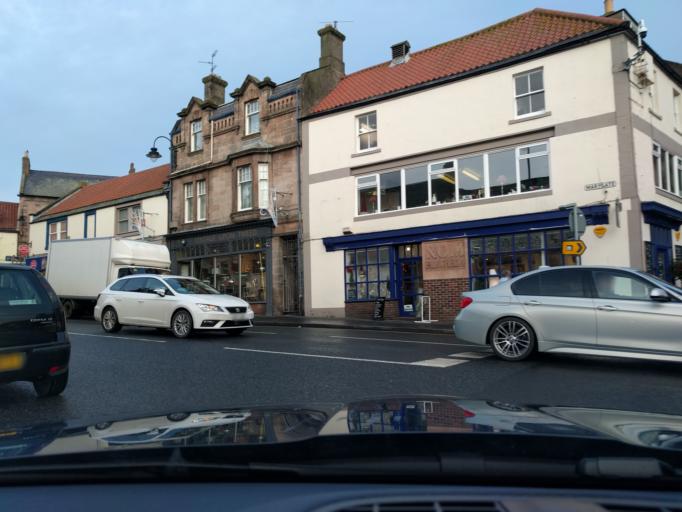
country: GB
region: England
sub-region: Northumberland
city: Berwick-Upon-Tweed
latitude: 55.7704
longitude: -2.0054
